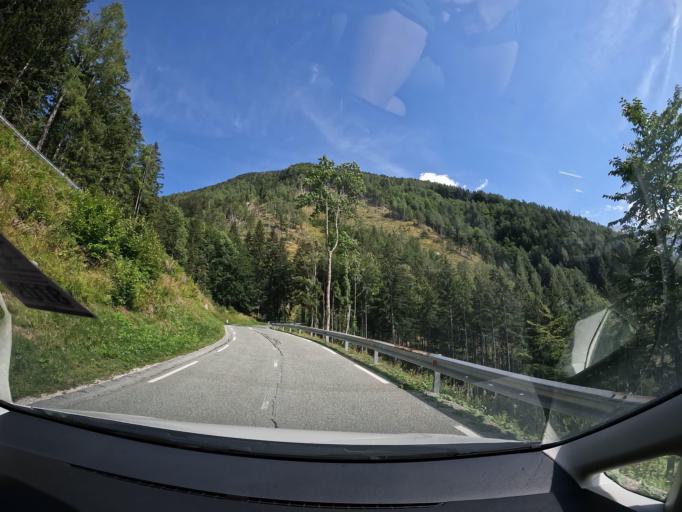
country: AT
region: Carinthia
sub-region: Politischer Bezirk Sankt Veit an der Glan
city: Liebenfels
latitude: 46.7055
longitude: 14.2880
